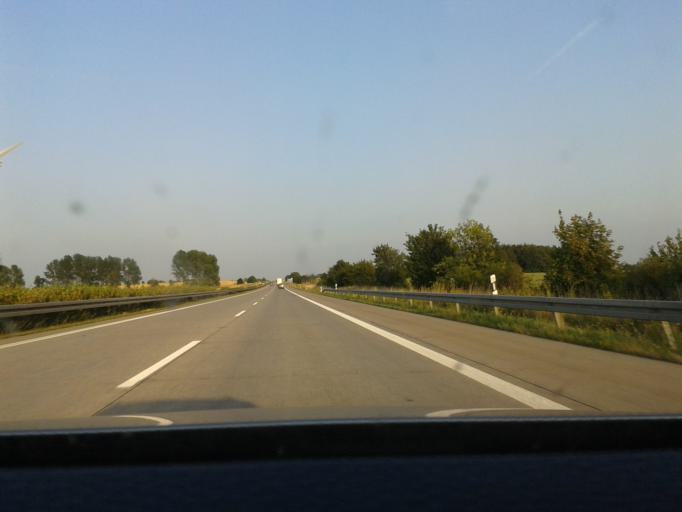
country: DE
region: Saxony
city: Bockelwitz
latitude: 51.1939
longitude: 12.9849
